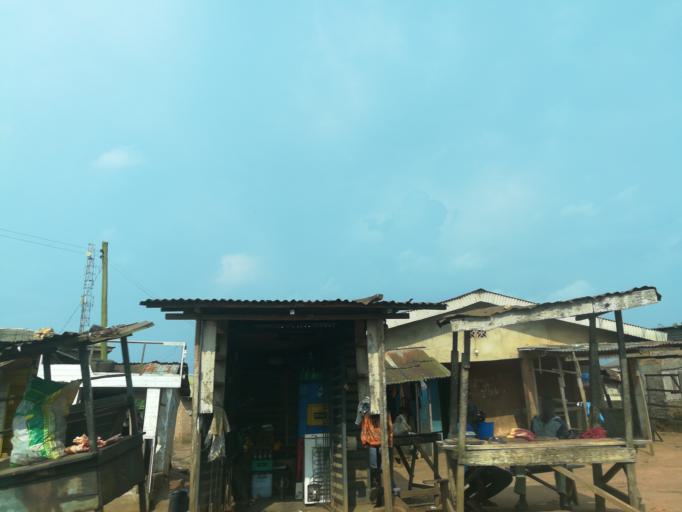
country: NG
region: Lagos
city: Ikorodu
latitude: 6.6674
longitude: 3.6713
